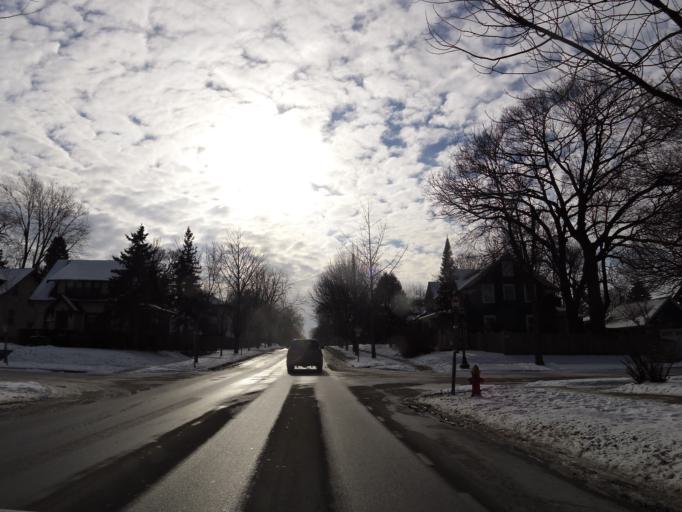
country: US
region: Minnesota
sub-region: Ramsey County
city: Falcon Heights
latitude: 44.9382
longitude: -93.1875
